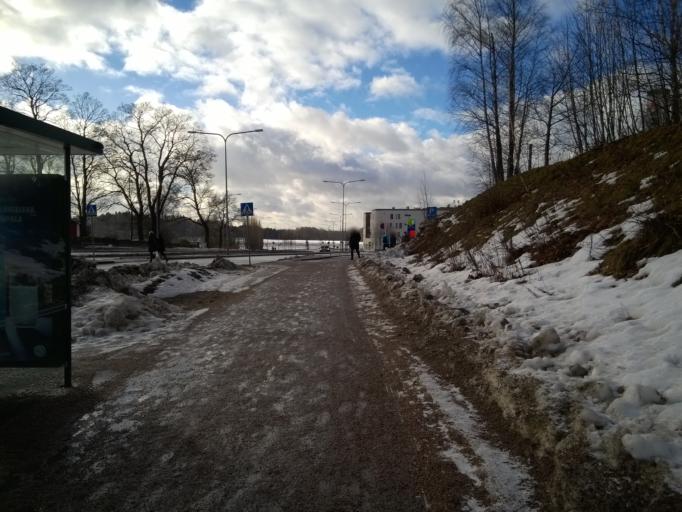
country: FI
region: Uusimaa
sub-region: Helsinki
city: Vantaa
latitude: 60.2277
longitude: 25.0111
